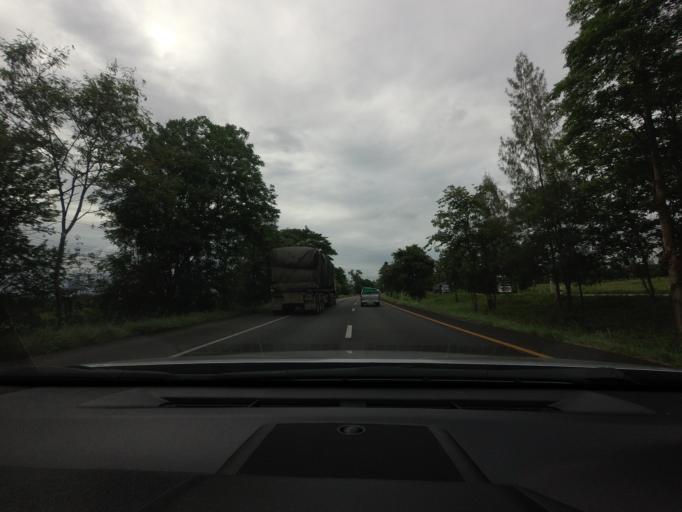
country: TH
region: Prachuap Khiri Khan
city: Hua Hin
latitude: 12.6288
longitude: 99.8574
